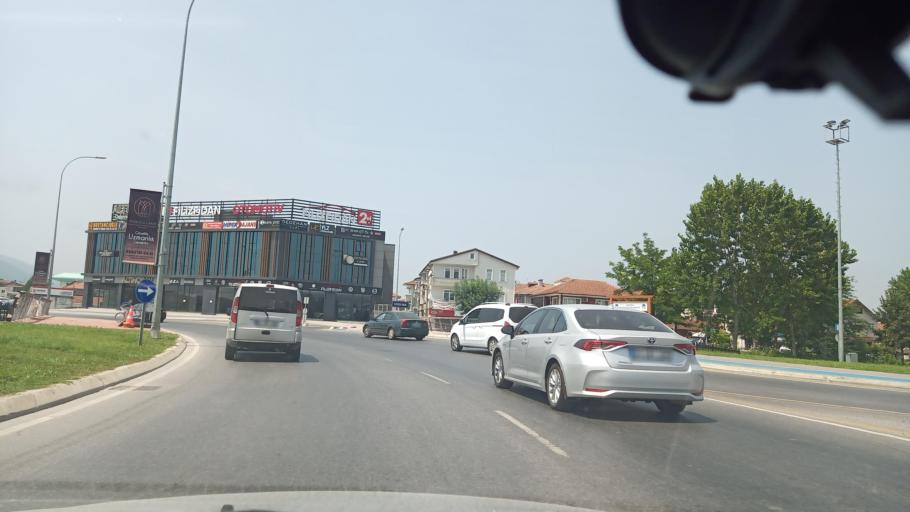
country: TR
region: Sakarya
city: Adapazari
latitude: 40.7883
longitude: 30.3736
